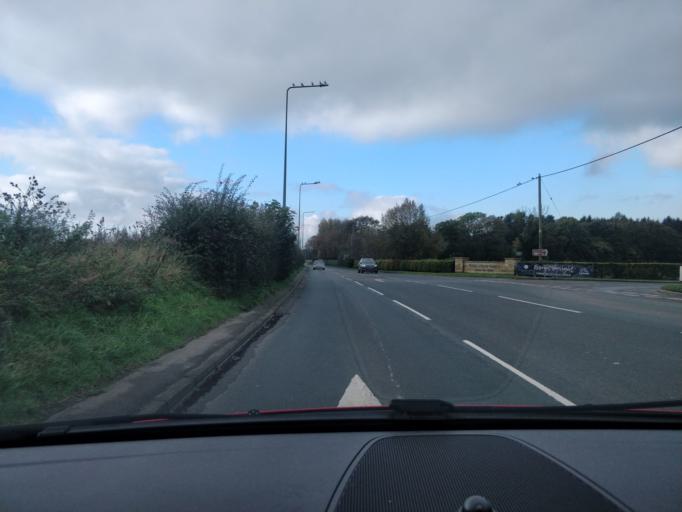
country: GB
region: England
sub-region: Lancashire
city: Ormskirk
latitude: 53.5848
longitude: -2.9090
